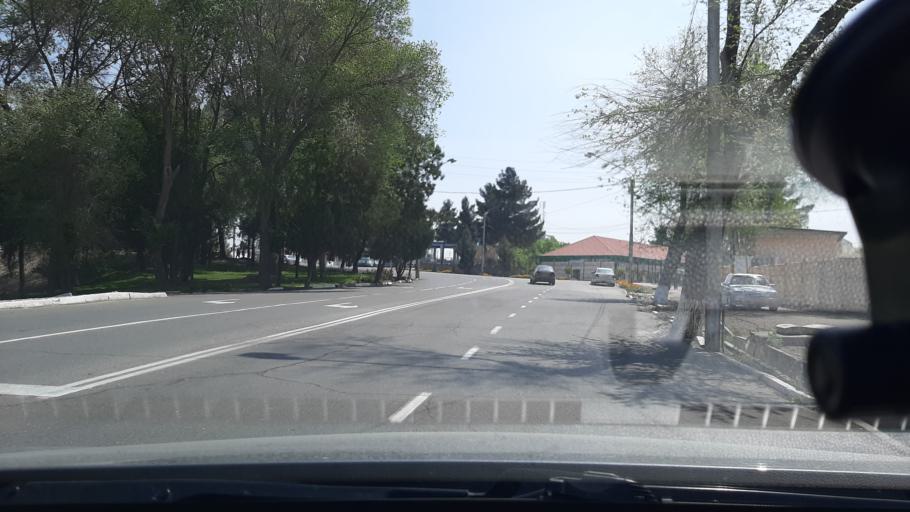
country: TJ
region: Viloyati Sughd
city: Khujand
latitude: 40.2927
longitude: 69.6390
